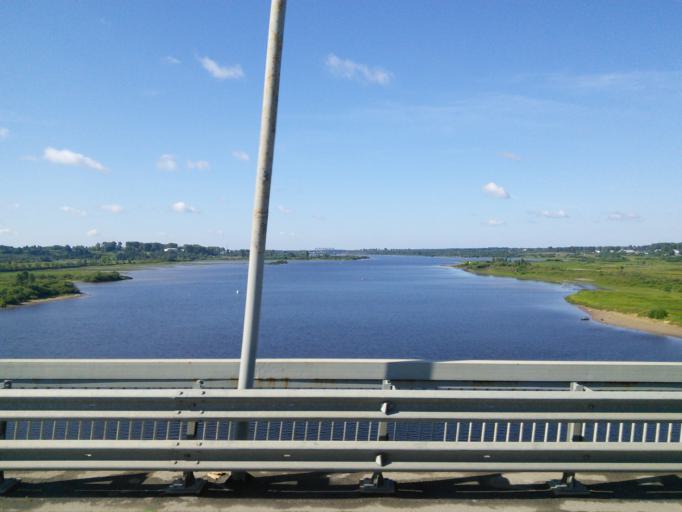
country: RU
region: Vologda
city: Sheksna
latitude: 59.2132
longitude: 38.4943
